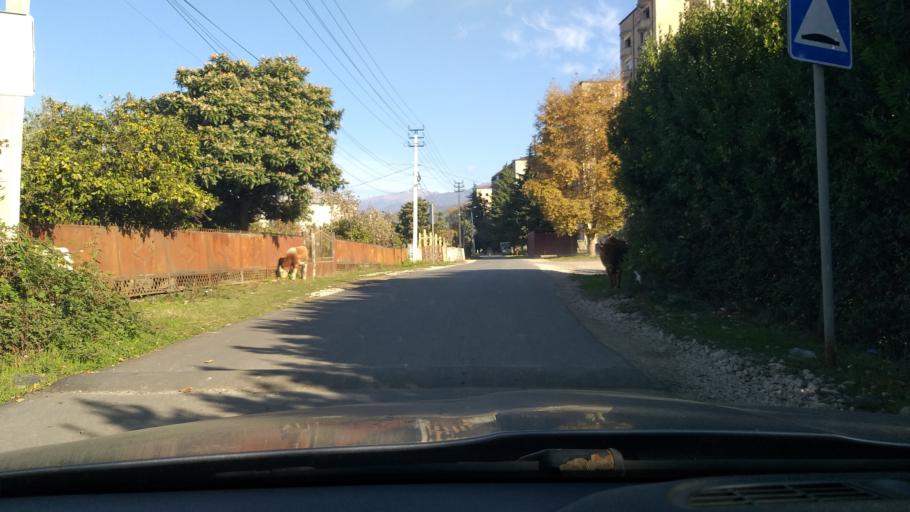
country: GE
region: Abkhazia
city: Sokhumi
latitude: 43.0160
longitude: 40.9617
